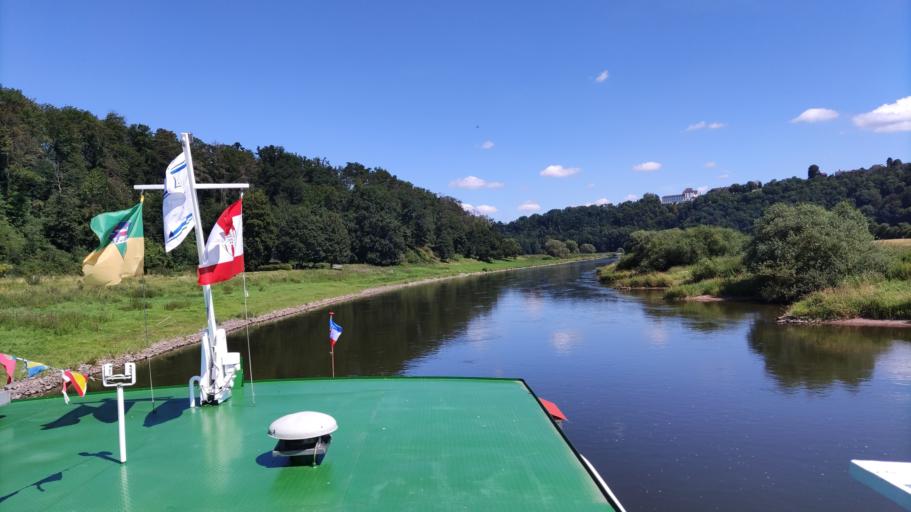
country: DE
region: Lower Saxony
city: Furstenberg
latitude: 51.7221
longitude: 9.3872
